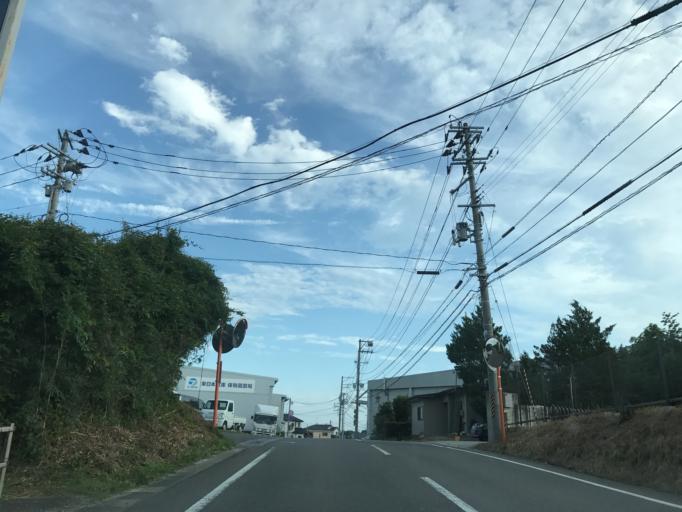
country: JP
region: Fukushima
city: Sukagawa
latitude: 37.3189
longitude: 140.3578
